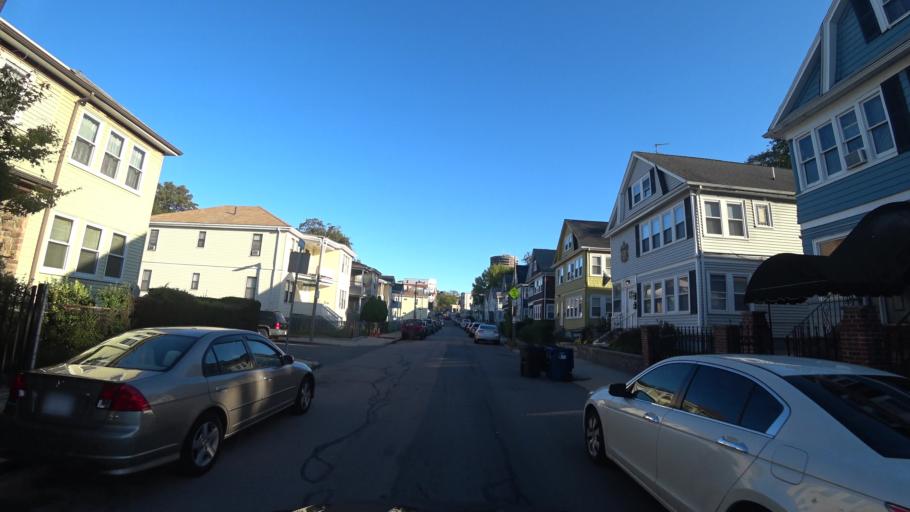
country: US
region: Massachusetts
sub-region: Suffolk County
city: Jamaica Plain
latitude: 42.3184
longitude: -71.1003
